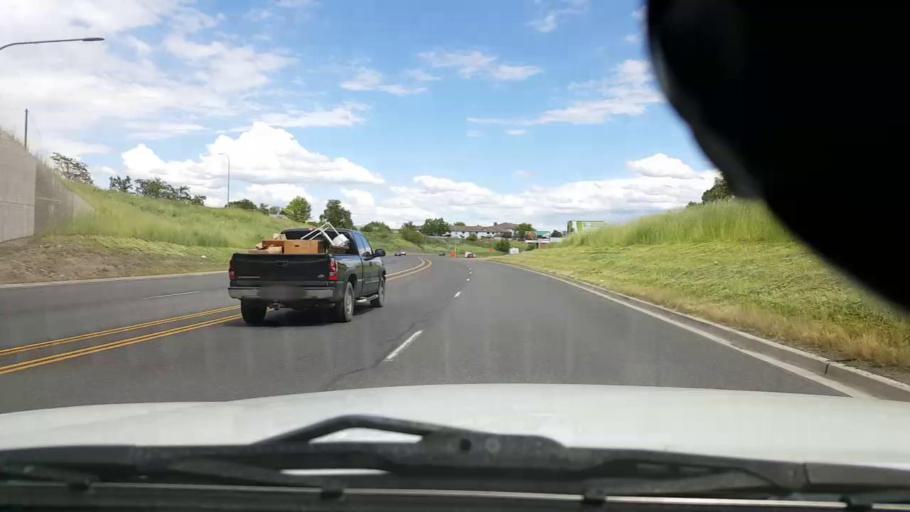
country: US
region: Washington
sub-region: Asotin County
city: West Clarkston-Highland
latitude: 46.4010
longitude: -117.0606
